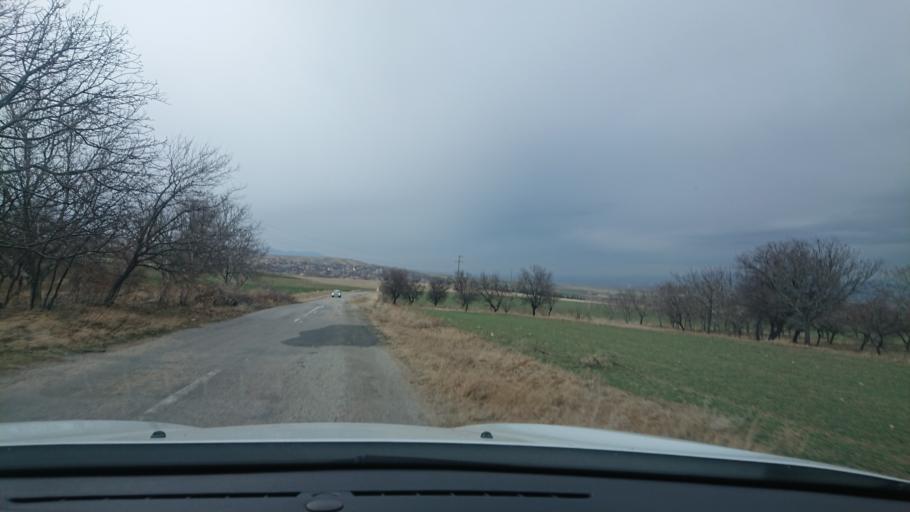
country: TR
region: Aksaray
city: Agacoren
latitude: 38.9469
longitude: 33.9063
